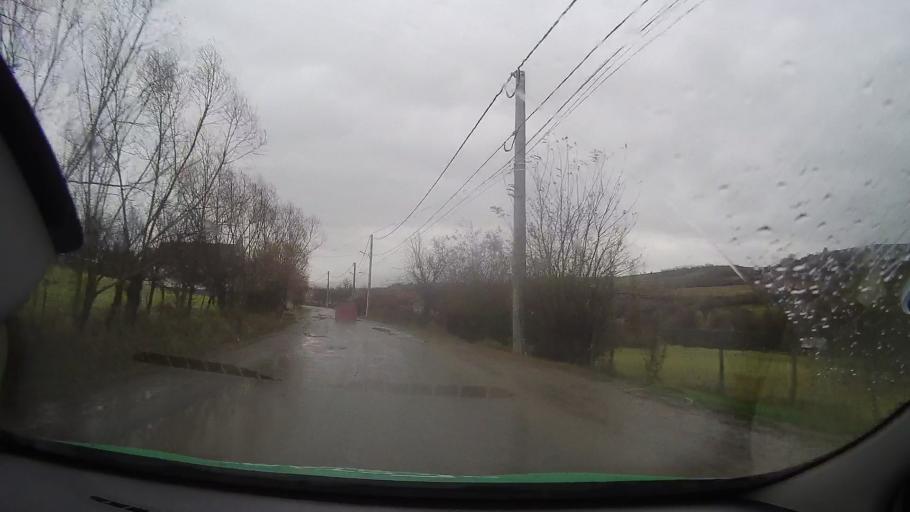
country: RO
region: Mures
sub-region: Comuna Vatava
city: Vatava
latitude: 46.9296
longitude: 24.7687
